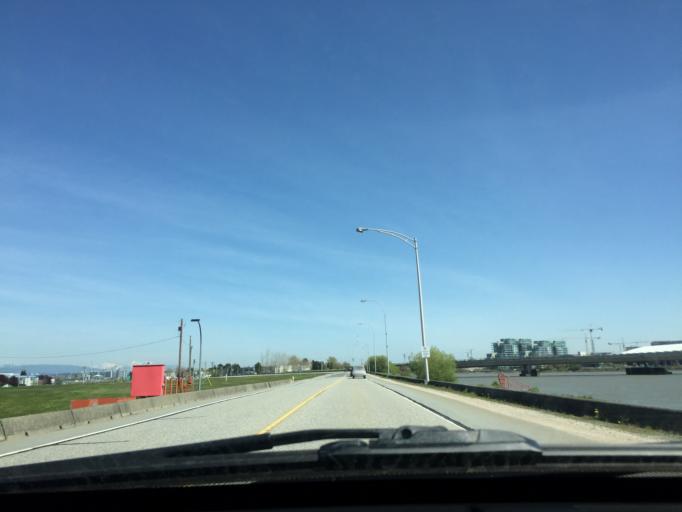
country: CA
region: British Columbia
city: Richmond
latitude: 49.1778
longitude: -123.1615
